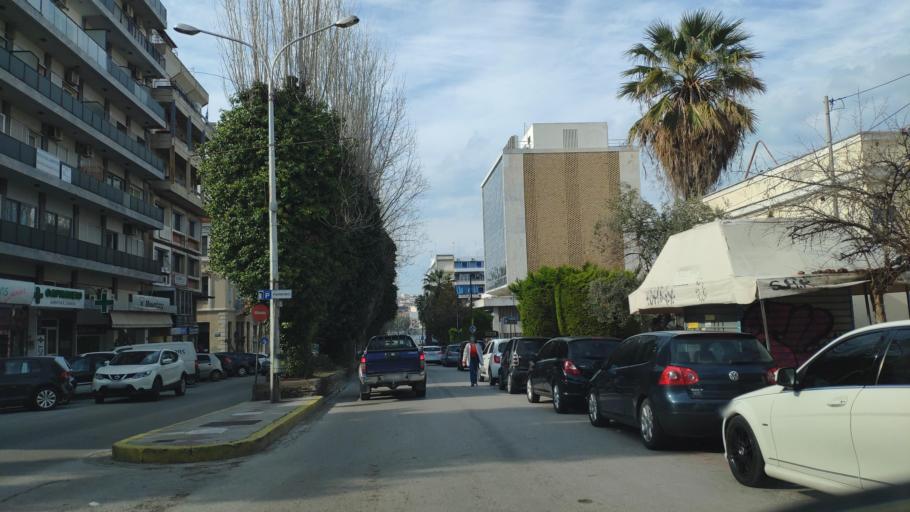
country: GR
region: Central Greece
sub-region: Nomos Evvoias
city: Chalkida
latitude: 38.4629
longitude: 23.5938
